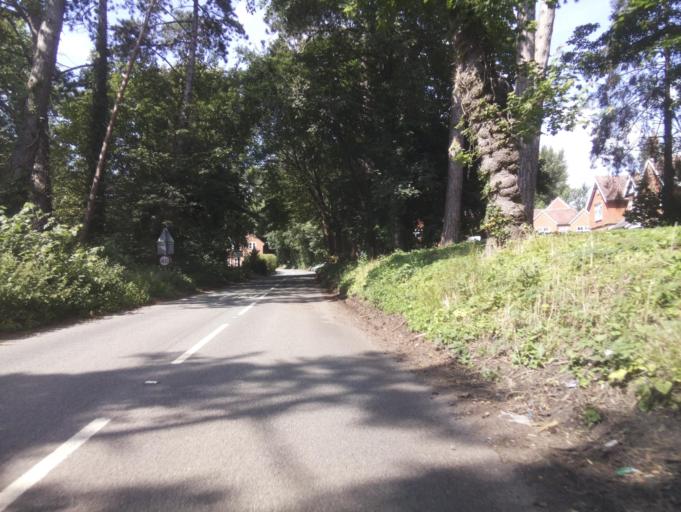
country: GB
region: England
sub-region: West Berkshire
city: Newbury
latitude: 51.4211
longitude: -1.3301
